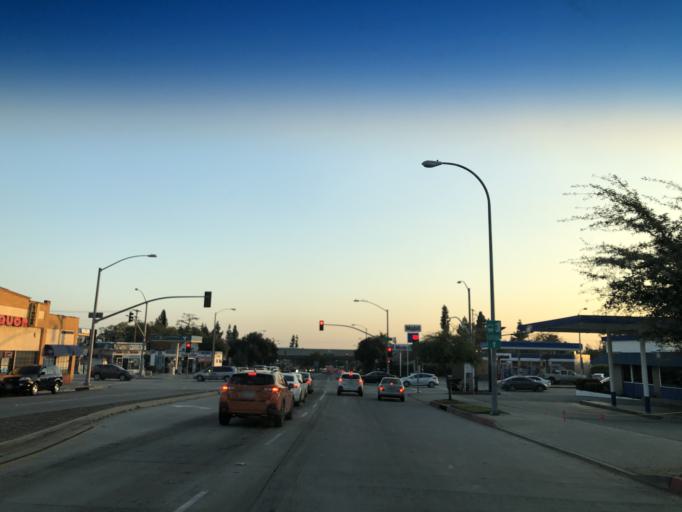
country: US
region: California
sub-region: Los Angeles County
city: East Pasadena
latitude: 34.1550
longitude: -118.1133
